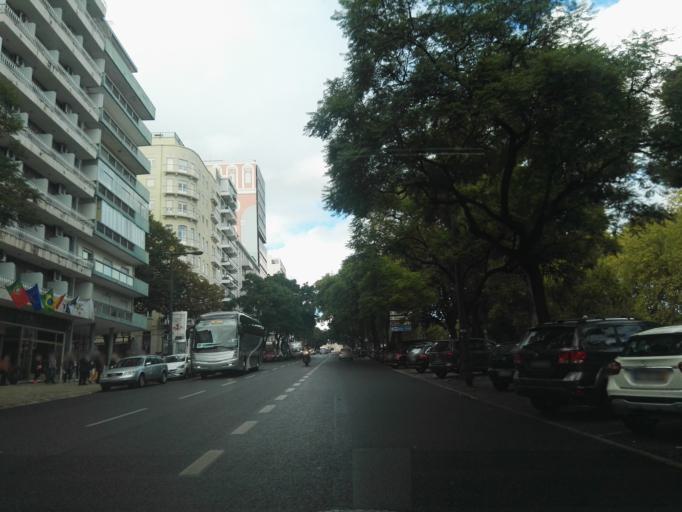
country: PT
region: Lisbon
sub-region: Lisbon
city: Lisbon
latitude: 38.7273
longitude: -9.1555
